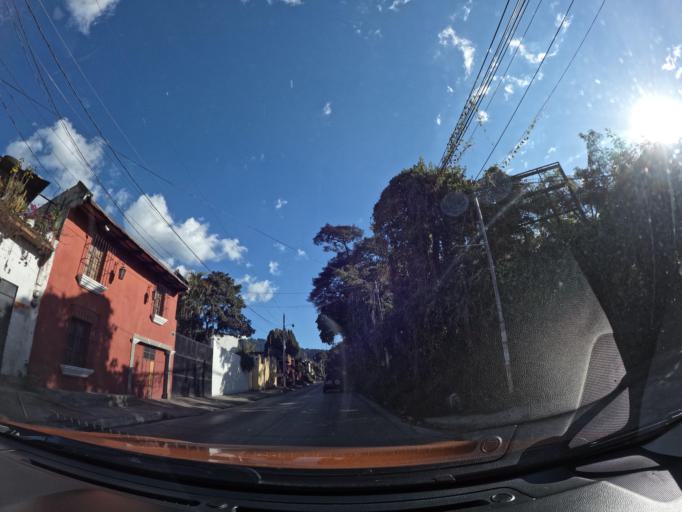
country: GT
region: Sacatepequez
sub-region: Municipio de Santa Maria de Jesus
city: Santa Maria de Jesus
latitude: 14.5304
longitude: -90.7275
